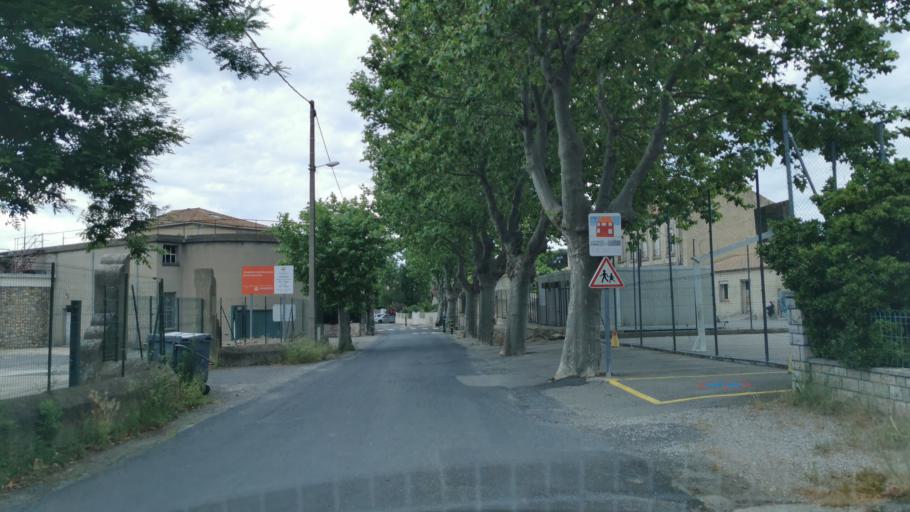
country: FR
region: Languedoc-Roussillon
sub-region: Departement de l'Aude
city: Moussan
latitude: 43.2297
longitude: 2.9500
